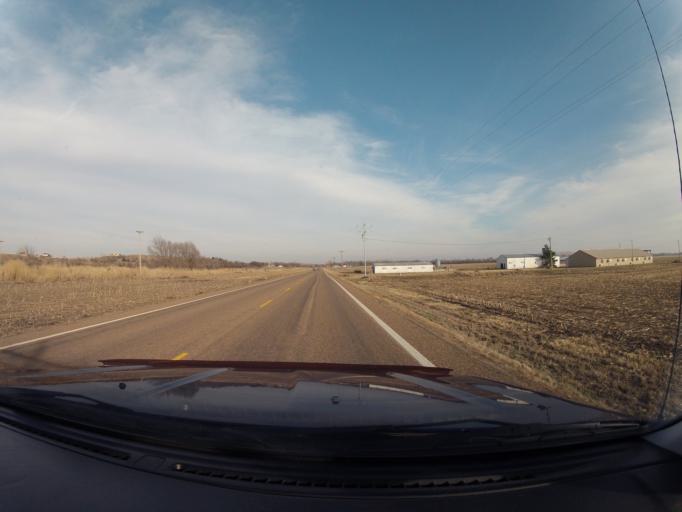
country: US
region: Kansas
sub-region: Pottawatomie County
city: Saint Marys
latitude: 39.2167
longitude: -96.1387
